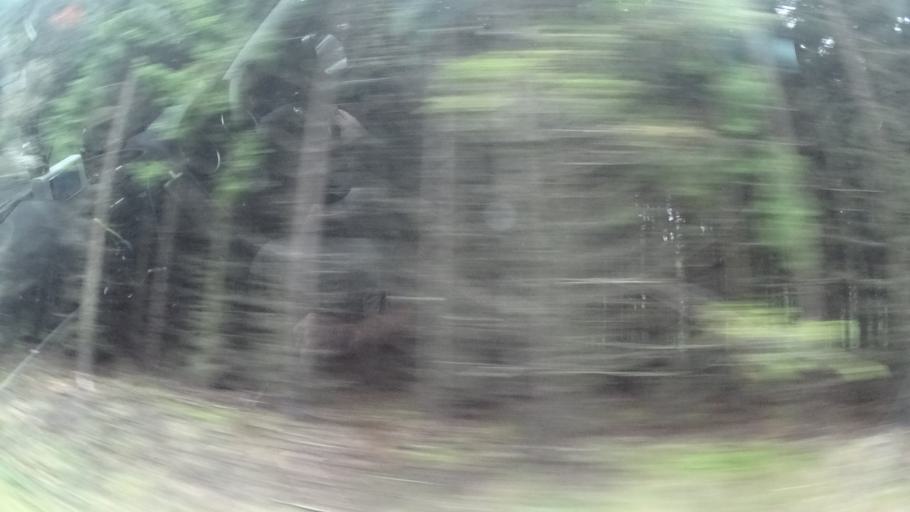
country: DE
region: Thuringia
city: Remptendorf
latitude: 50.5363
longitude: 11.6026
